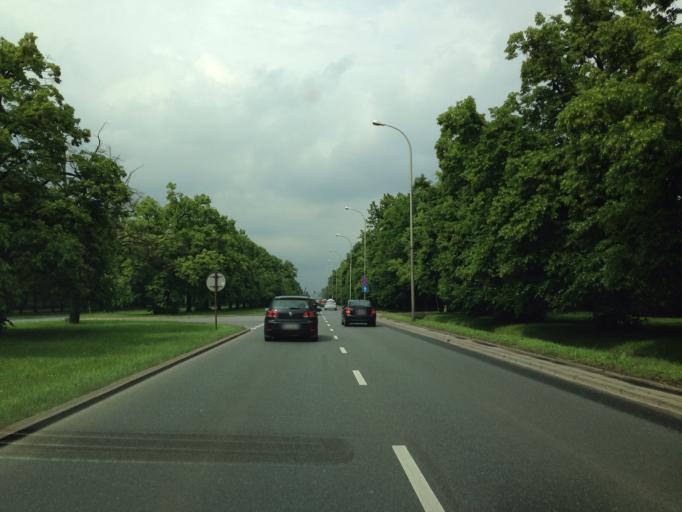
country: PL
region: Masovian Voivodeship
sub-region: Warszawa
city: Wlochy
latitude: 52.1857
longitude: 20.9797
